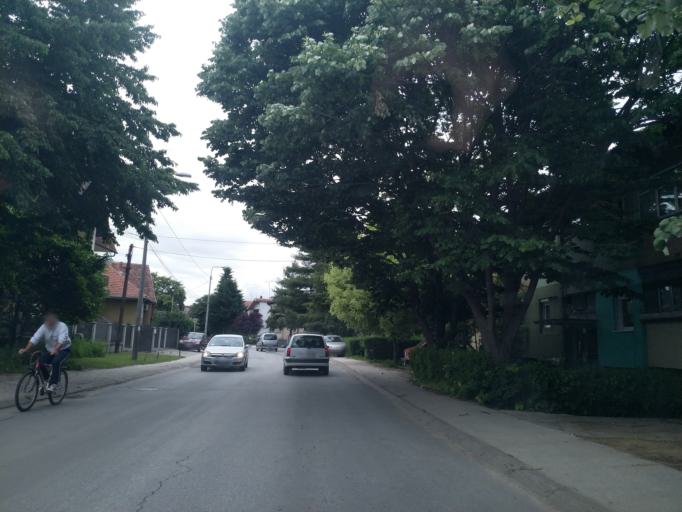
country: RS
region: Central Serbia
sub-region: Pomoravski Okrug
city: Jagodina
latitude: 43.9748
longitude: 21.2727
